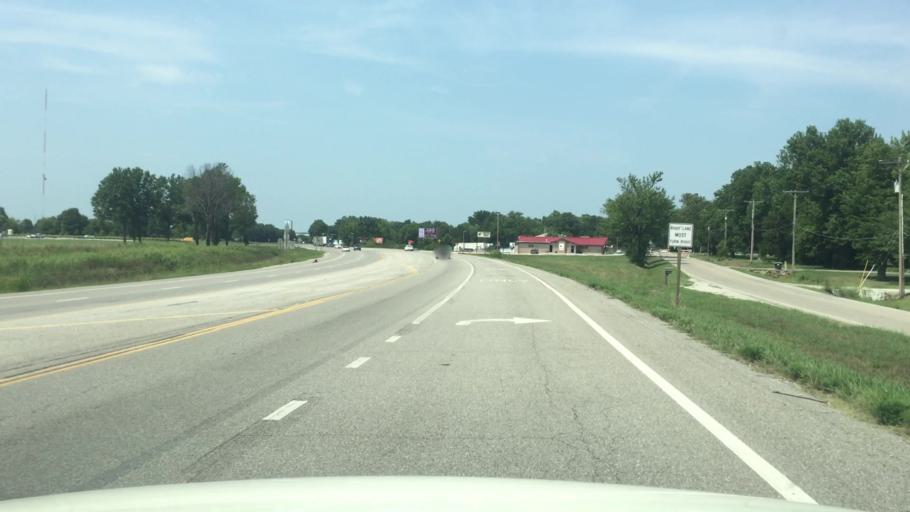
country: US
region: Kansas
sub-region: Crawford County
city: Pittsburg
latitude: 37.3414
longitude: -94.7054
